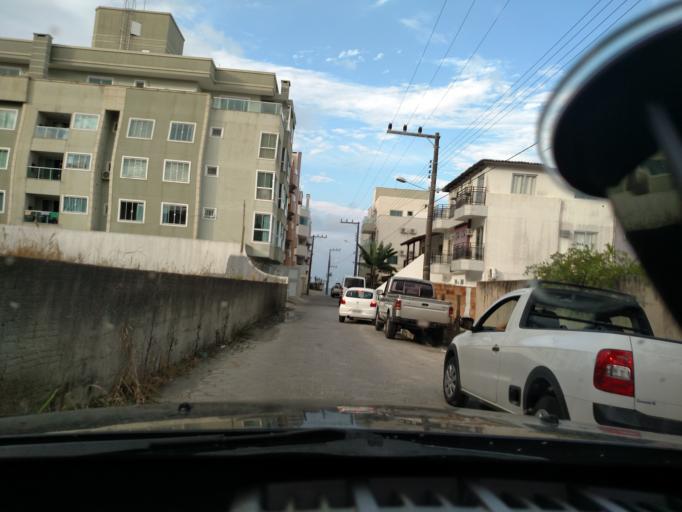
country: BR
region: Santa Catarina
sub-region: Porto Belo
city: Porto Belo
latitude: -27.1379
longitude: -48.5134
